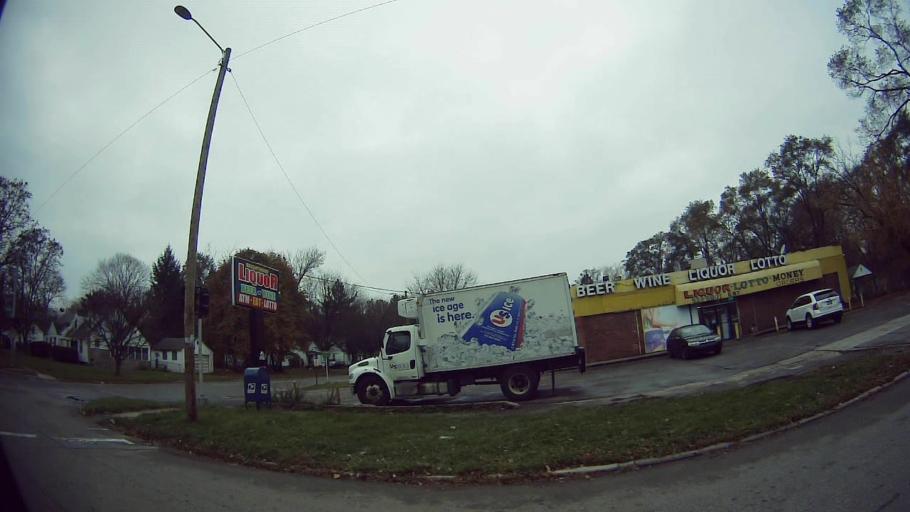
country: US
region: Michigan
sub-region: Wayne County
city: Redford
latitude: 42.3933
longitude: -83.2567
